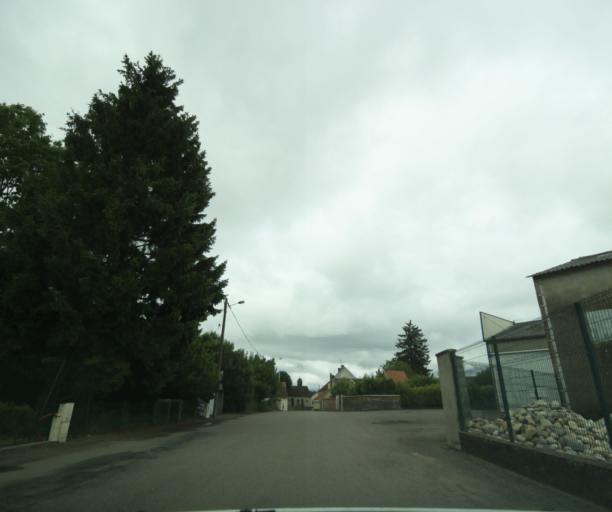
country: FR
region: Bourgogne
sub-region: Departement de Saone-et-Loire
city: Charolles
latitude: 46.4320
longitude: 4.2695
